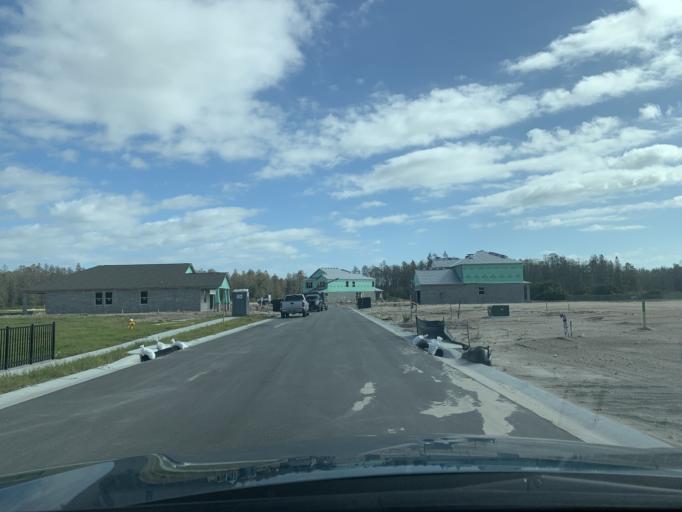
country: US
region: Florida
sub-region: Pasco County
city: Trinity
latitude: 28.1979
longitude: -82.6713
